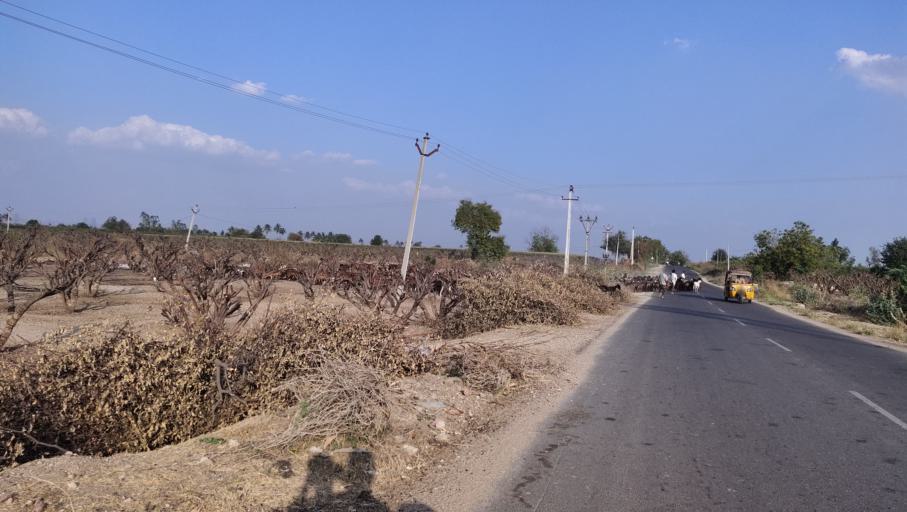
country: IN
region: Andhra Pradesh
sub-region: Anantapur
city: Tadpatri
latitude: 14.9508
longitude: 77.8880
